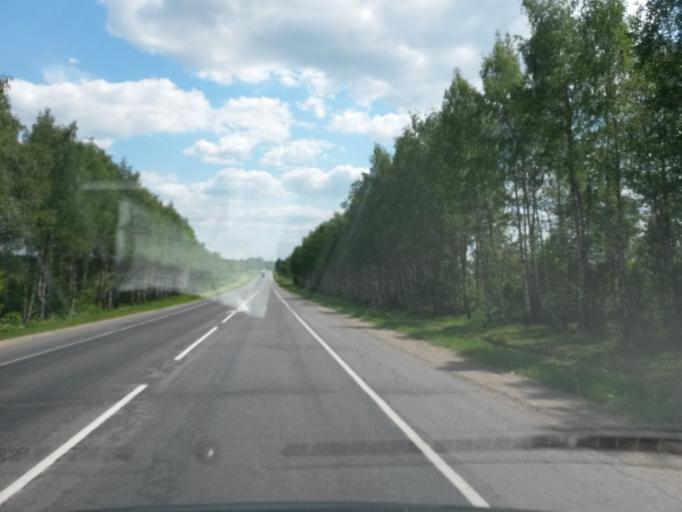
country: RU
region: Jaroslavl
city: Yaroslavl
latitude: 57.5579
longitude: 39.8618
